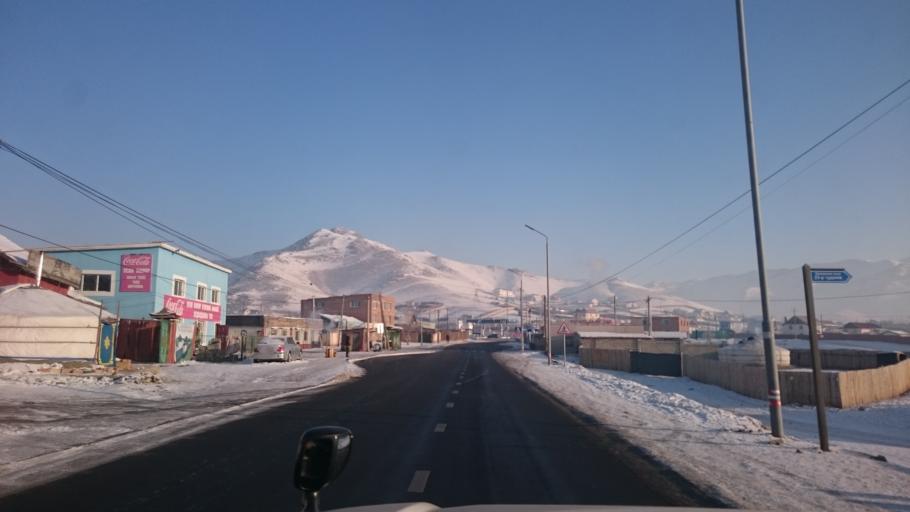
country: MN
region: Ulaanbaatar
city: Ulaanbaatar
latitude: 47.9267
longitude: 107.1429
